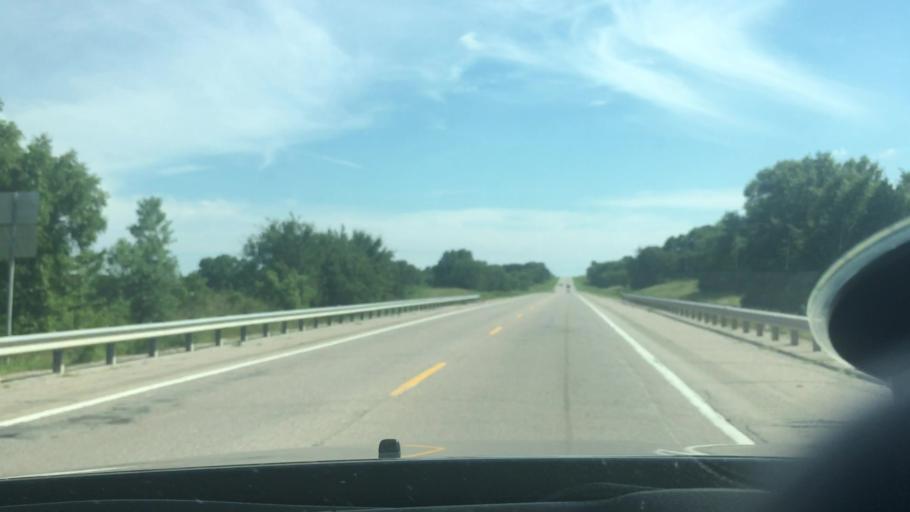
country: US
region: Oklahoma
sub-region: Seminole County
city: Maud
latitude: 35.1273
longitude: -96.6790
